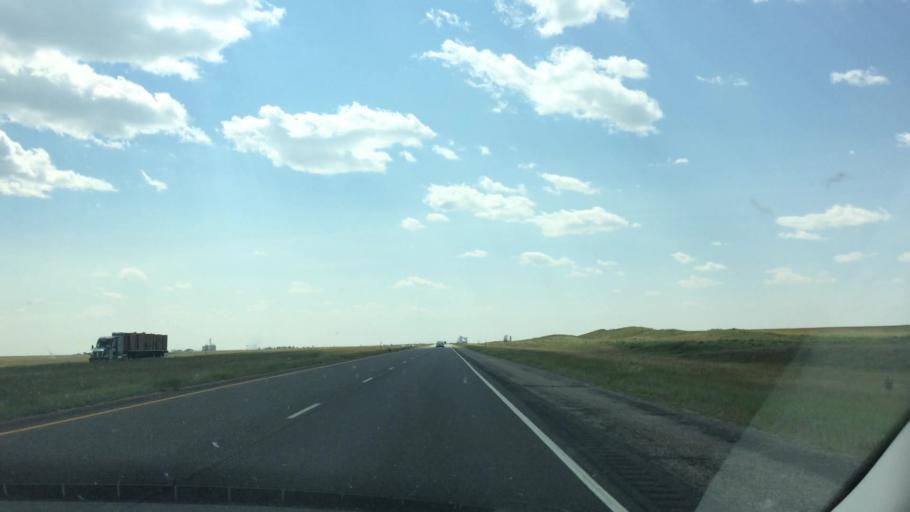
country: US
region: Colorado
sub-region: Lincoln County
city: Hugo
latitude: 39.2850
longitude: -103.2247
